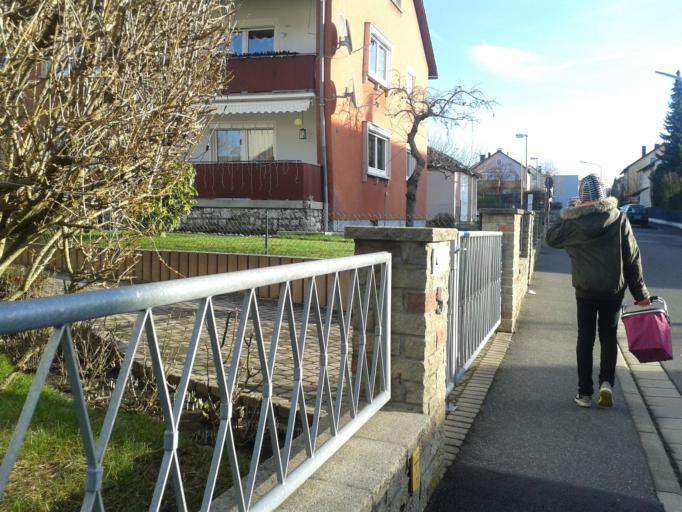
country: DE
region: Bavaria
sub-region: Upper Franconia
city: Kronach
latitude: 50.2363
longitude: 11.3338
